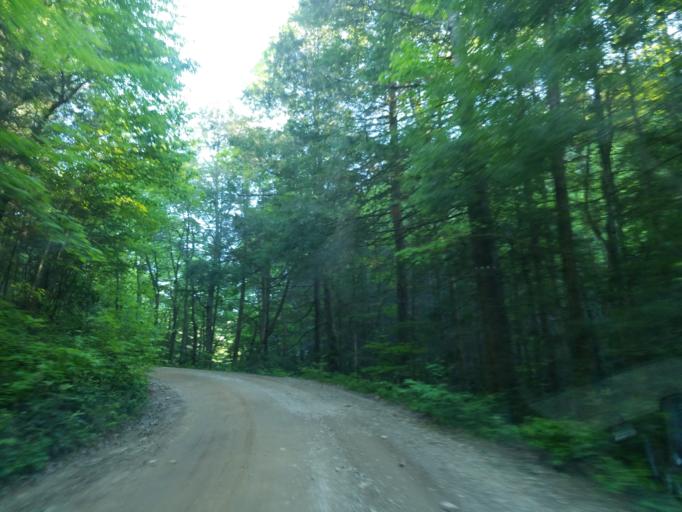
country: US
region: Georgia
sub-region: Lumpkin County
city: Dahlonega
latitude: 34.6852
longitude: -84.1405
